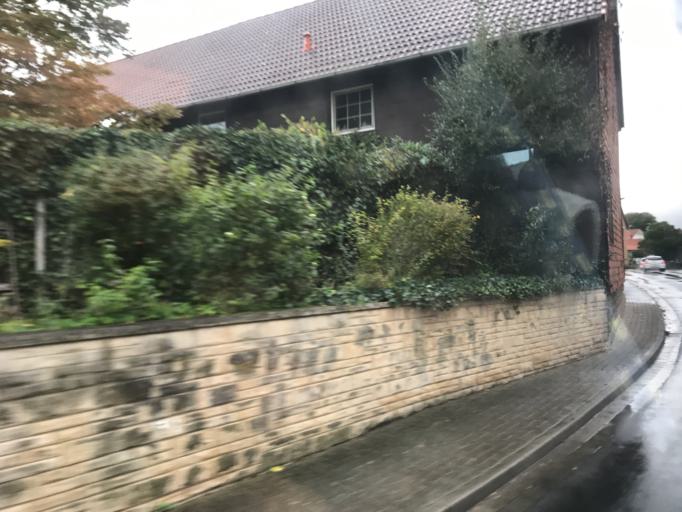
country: DE
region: Lower Saxony
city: Goettingen
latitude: 51.4863
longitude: 9.9766
